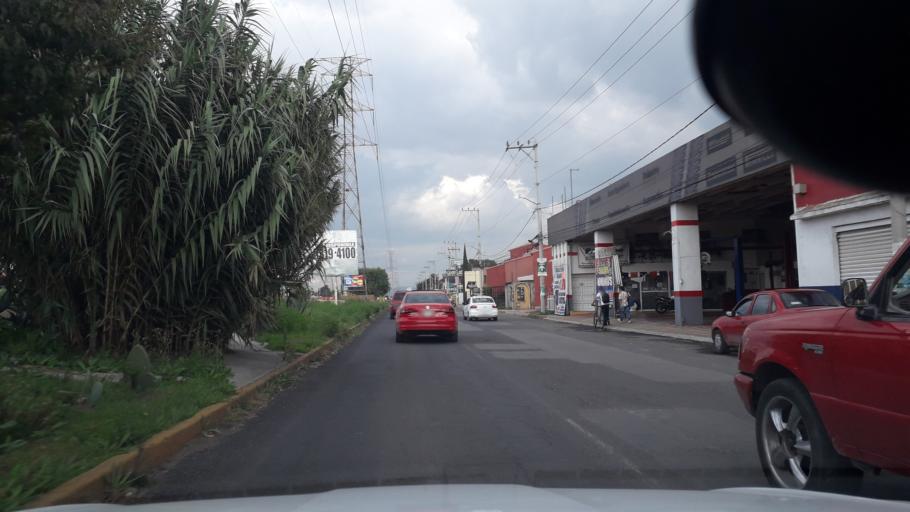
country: MX
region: Mexico
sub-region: Tultitlan
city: Fuentes del Valle
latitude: 19.6409
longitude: -99.1270
